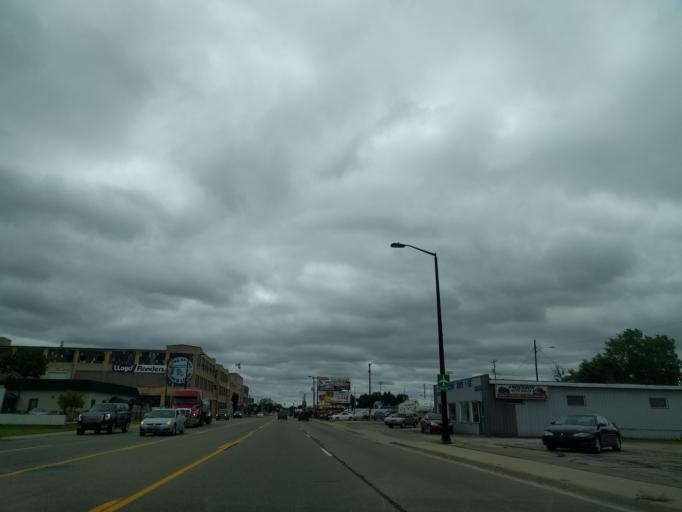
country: US
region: Michigan
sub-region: Menominee County
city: Menominee
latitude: 45.1282
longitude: -87.6130
